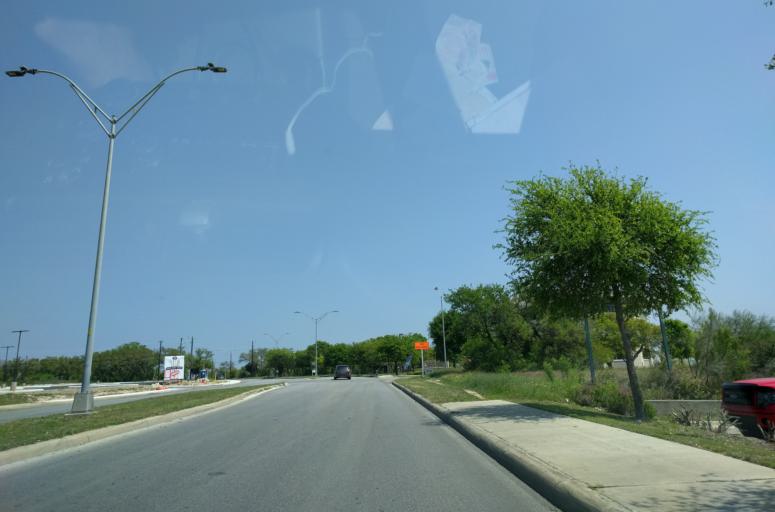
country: US
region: Texas
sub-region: Bexar County
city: Shavano Park
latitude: 29.5757
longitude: -98.5935
